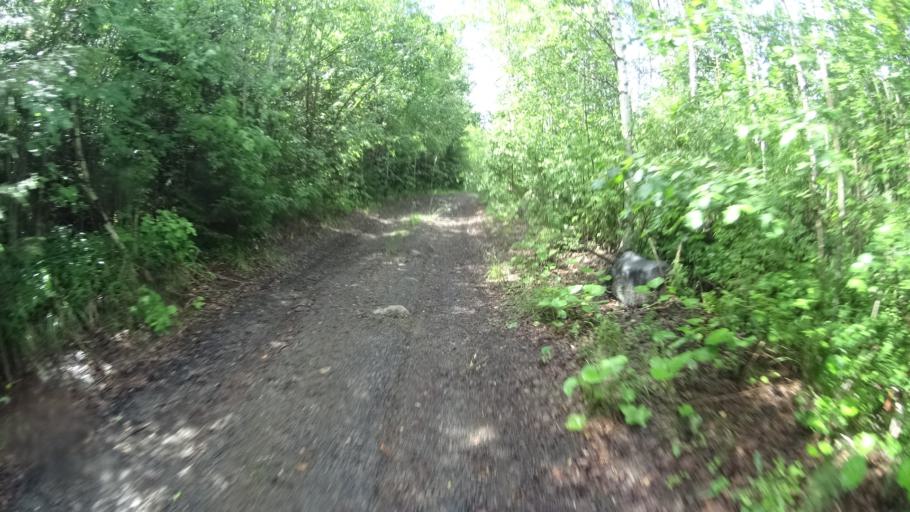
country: FI
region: Uusimaa
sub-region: Helsinki
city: Karkkila
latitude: 60.5856
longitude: 24.3246
